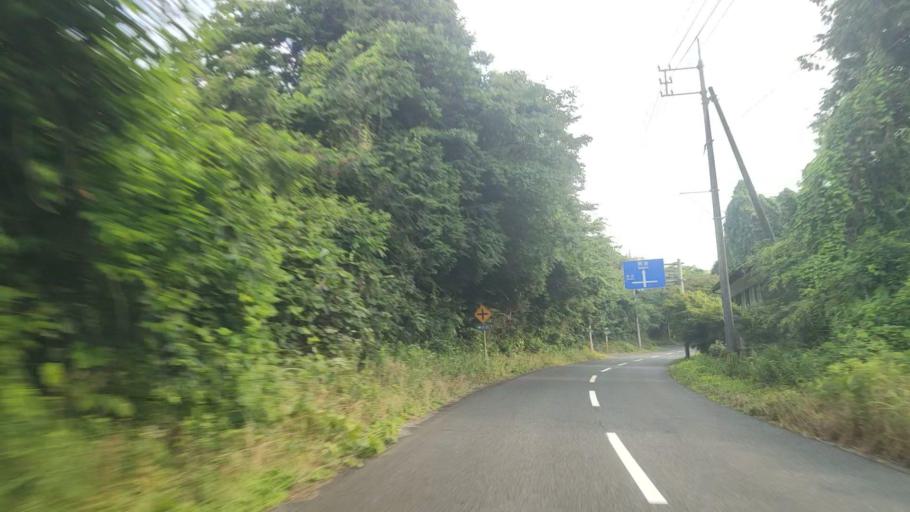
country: JP
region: Tottori
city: Kurayoshi
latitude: 35.4056
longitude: 133.7791
